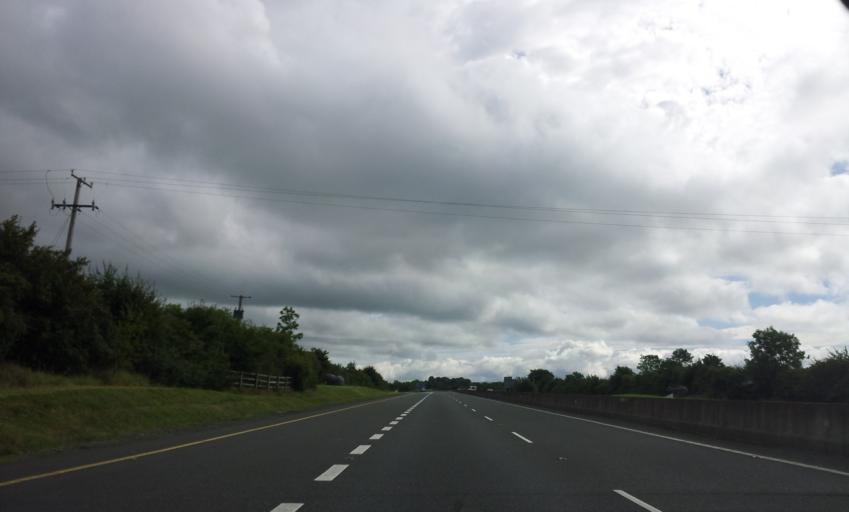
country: IE
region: Munster
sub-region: North Tipperary
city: Nenagh
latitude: 52.8485
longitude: -8.1698
